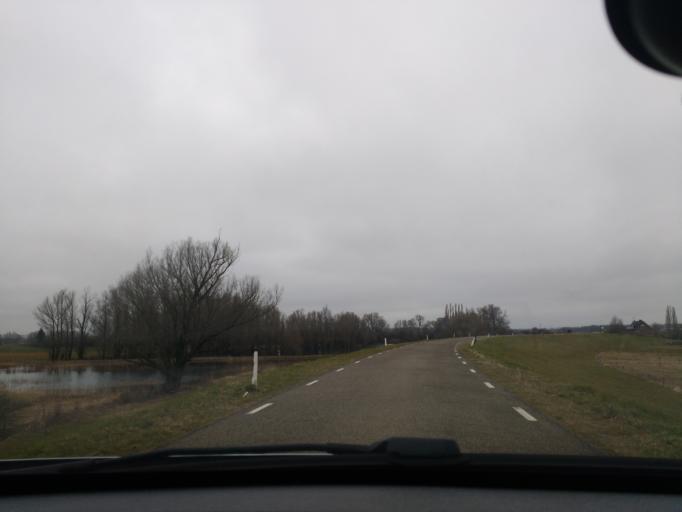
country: NL
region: Gelderland
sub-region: Gemeente Groesbeek
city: Berg en Dal
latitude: 51.8648
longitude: 5.9019
